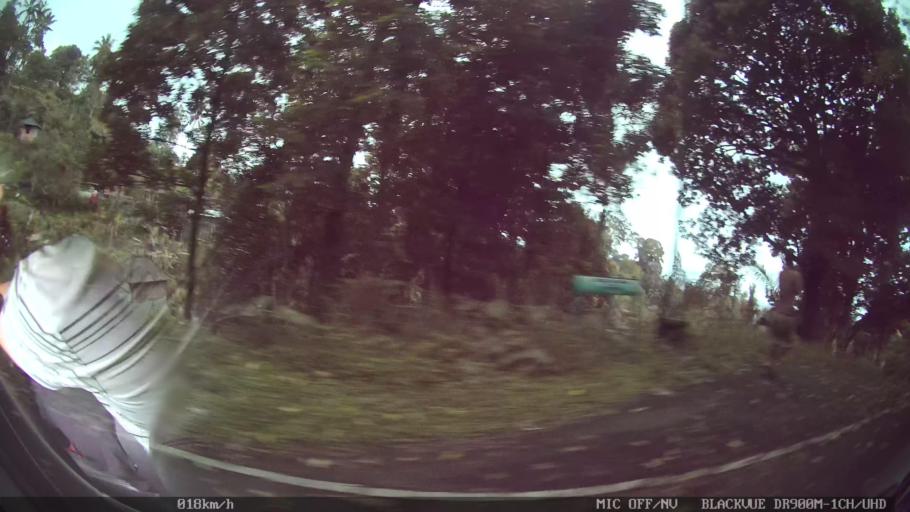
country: ID
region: Bali
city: Peneng
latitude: -8.3690
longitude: 115.2169
